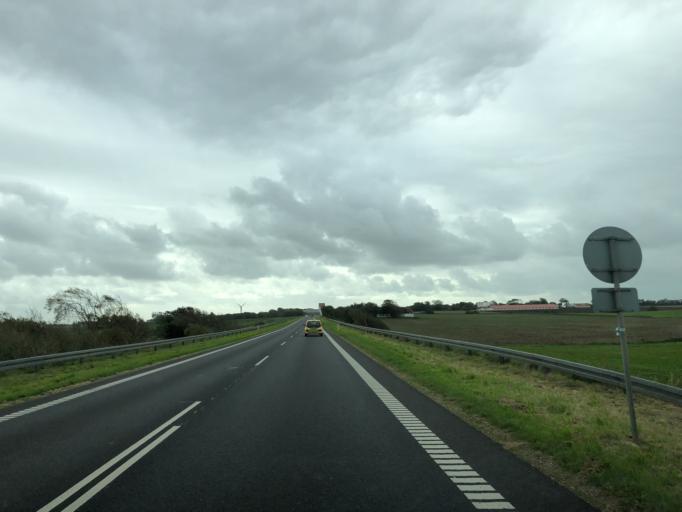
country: DK
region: North Denmark
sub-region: Thisted Kommune
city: Thisted
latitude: 56.8811
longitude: 8.5939
